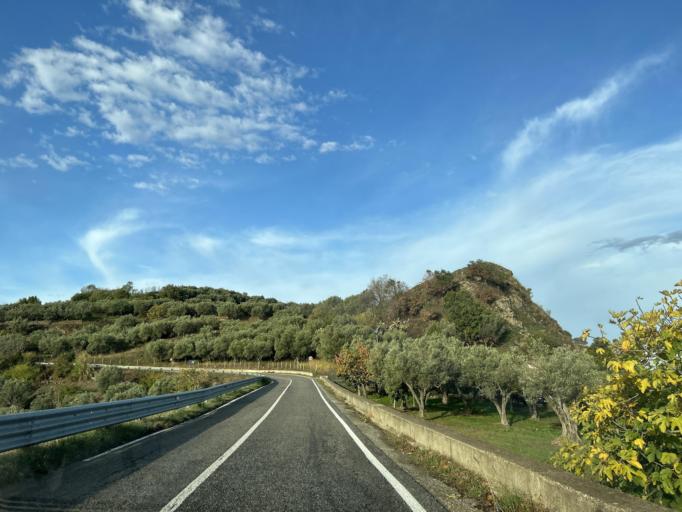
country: IT
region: Calabria
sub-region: Provincia di Catanzaro
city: Montauro
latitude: 38.7630
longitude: 16.5187
